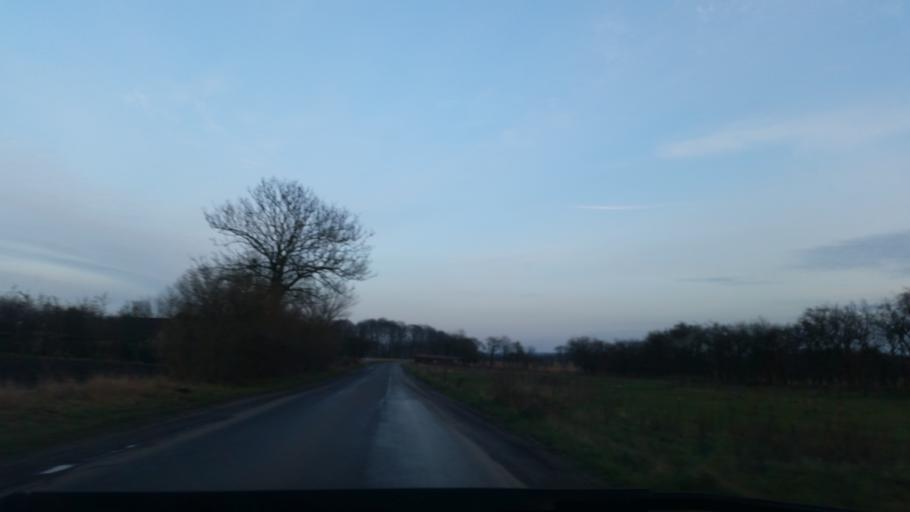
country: DK
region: South Denmark
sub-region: Vejen Kommune
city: Holsted
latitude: 55.3838
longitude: 8.9308
